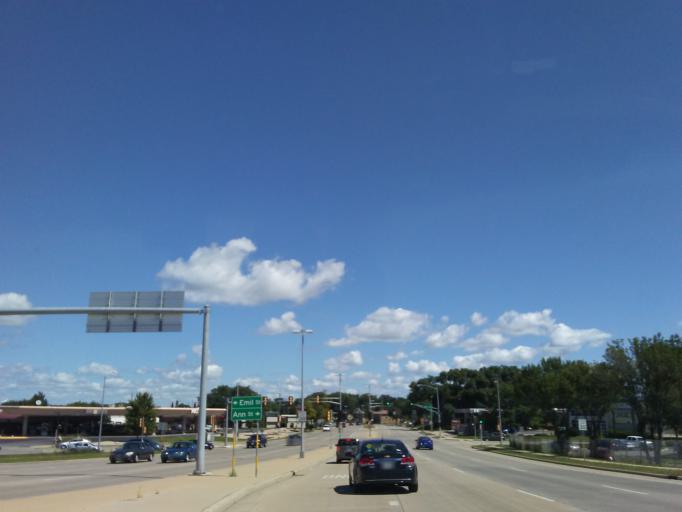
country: US
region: Wisconsin
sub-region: Dane County
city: Madison
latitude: 43.0357
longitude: -89.4059
